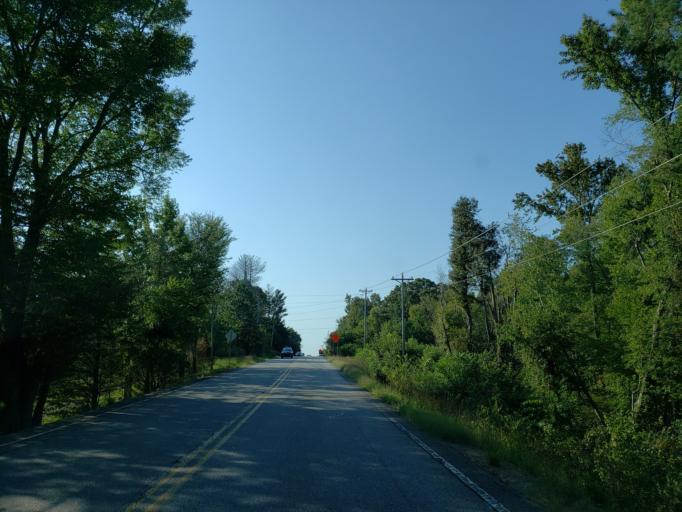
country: US
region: Tennessee
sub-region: Bradley County
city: Wildwood Lake
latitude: 34.9809
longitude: -84.7327
